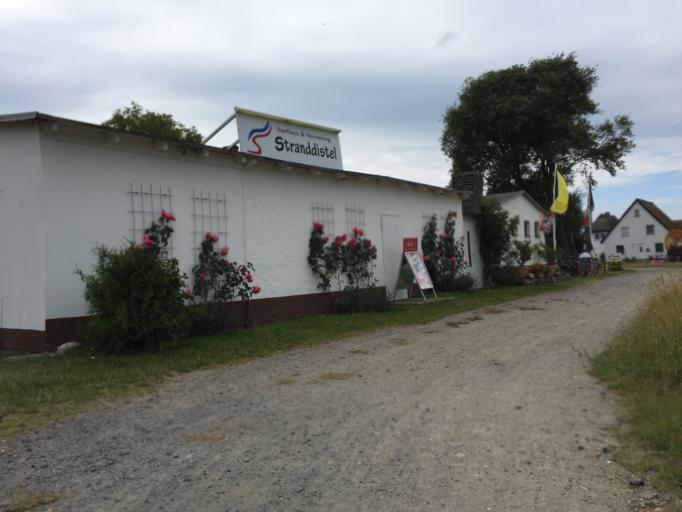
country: DE
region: Mecklenburg-Vorpommern
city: Hiddensee
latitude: 54.5223
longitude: 13.0859
